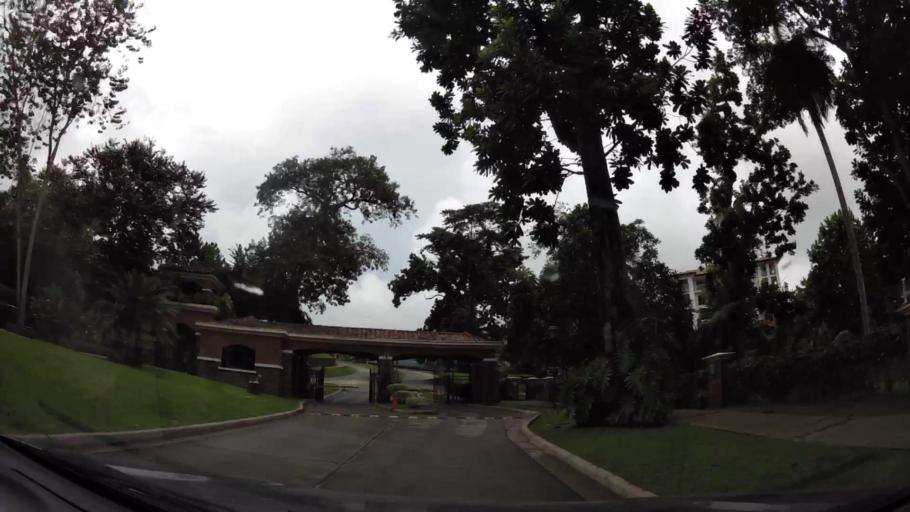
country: PA
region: Panama
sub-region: Distrito de Panama
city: Ancon
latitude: 8.9937
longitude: -79.5599
